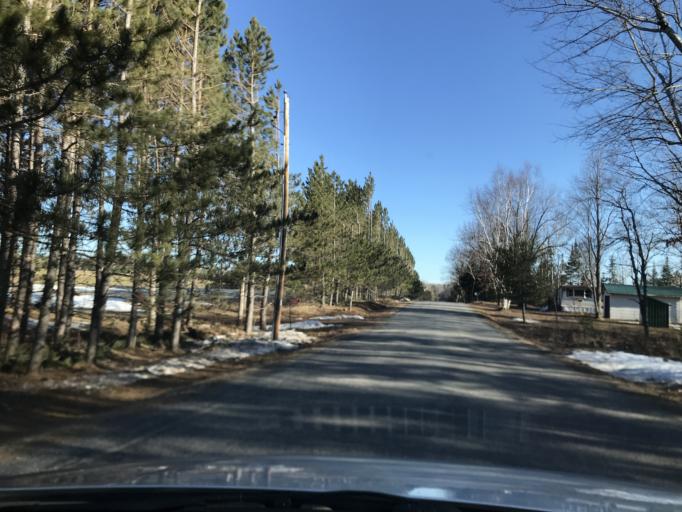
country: US
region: Wisconsin
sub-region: Marinette County
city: Niagara
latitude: 45.3593
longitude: -88.0296
